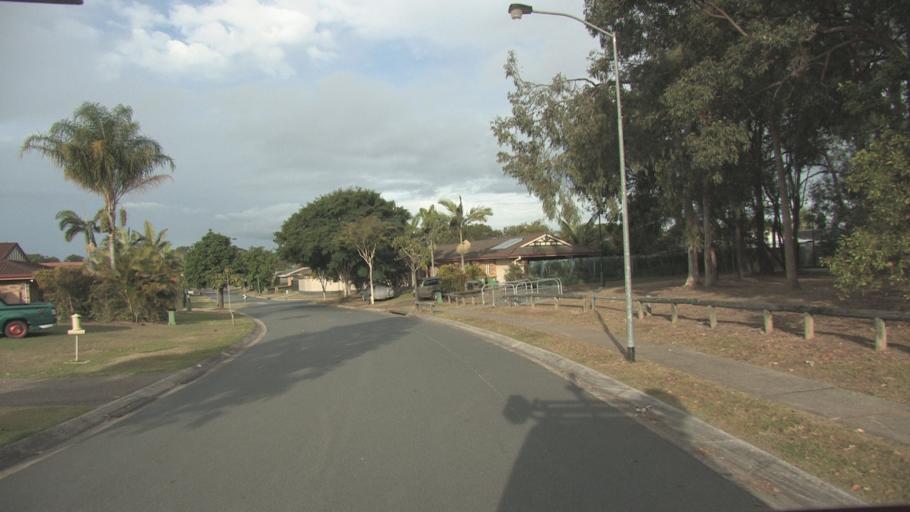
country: AU
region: Queensland
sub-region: Logan
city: Park Ridge South
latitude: -27.6776
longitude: 153.0184
